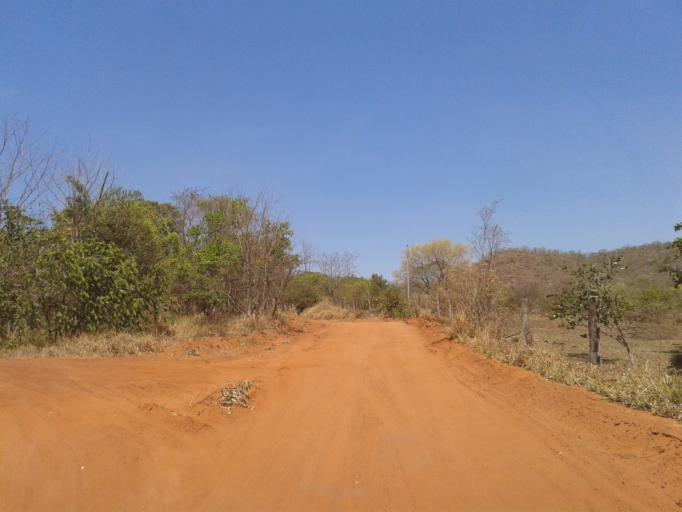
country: BR
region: Minas Gerais
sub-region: Ituiutaba
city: Ituiutaba
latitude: -19.0869
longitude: -49.2997
